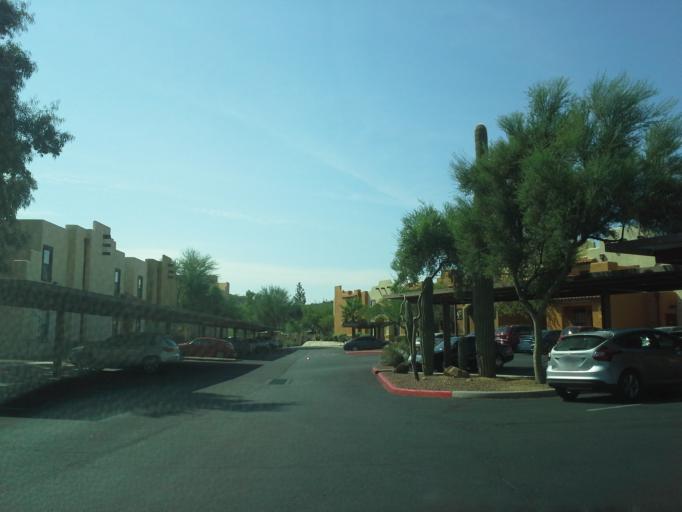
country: US
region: Arizona
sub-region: Pima County
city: South Tucson
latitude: 32.2194
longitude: -111.0275
